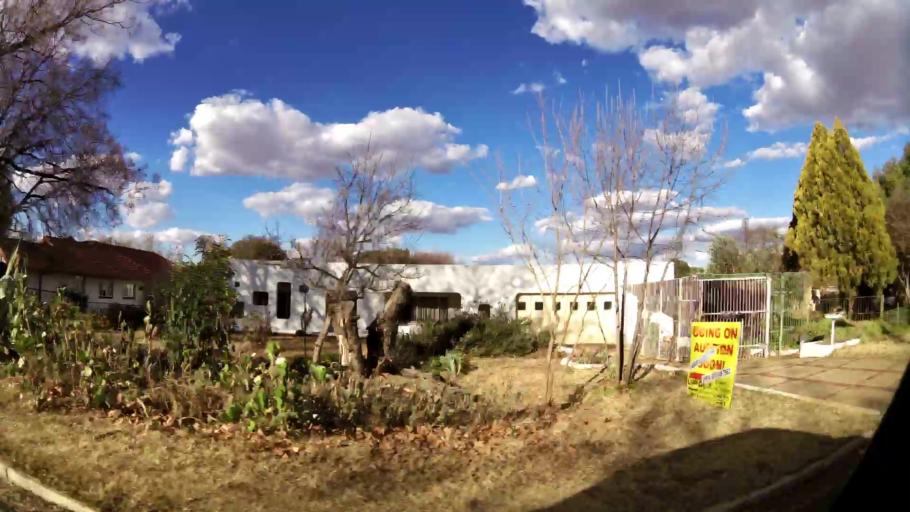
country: ZA
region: North-West
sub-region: Dr Kenneth Kaunda District Municipality
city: Potchefstroom
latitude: -26.6930
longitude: 27.0974
